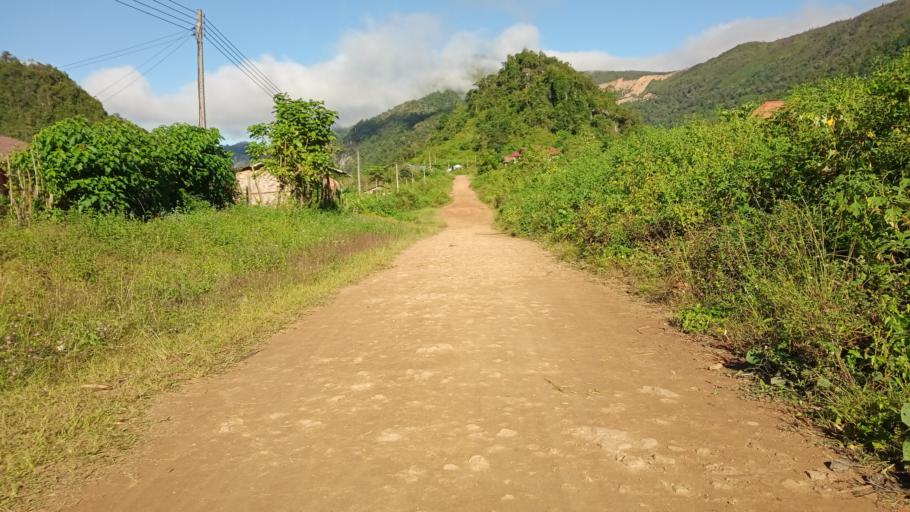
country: LA
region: Xiangkhoang
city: Phonsavan
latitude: 19.1148
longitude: 102.9123
